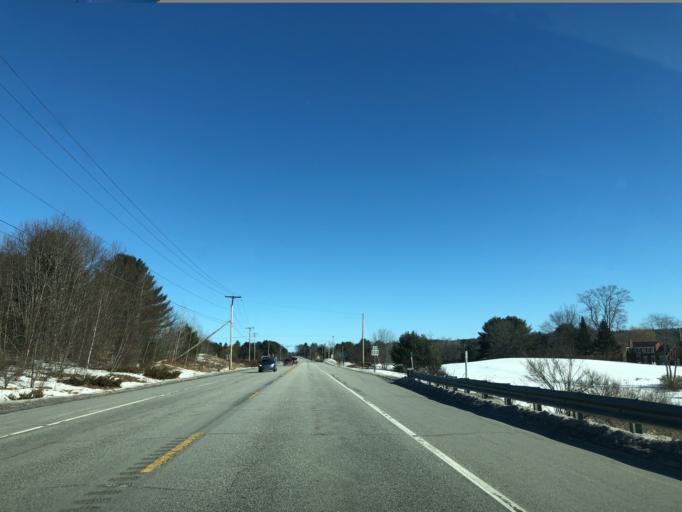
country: US
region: Maine
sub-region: Cumberland County
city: New Gloucester
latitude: 44.0222
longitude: -70.2792
